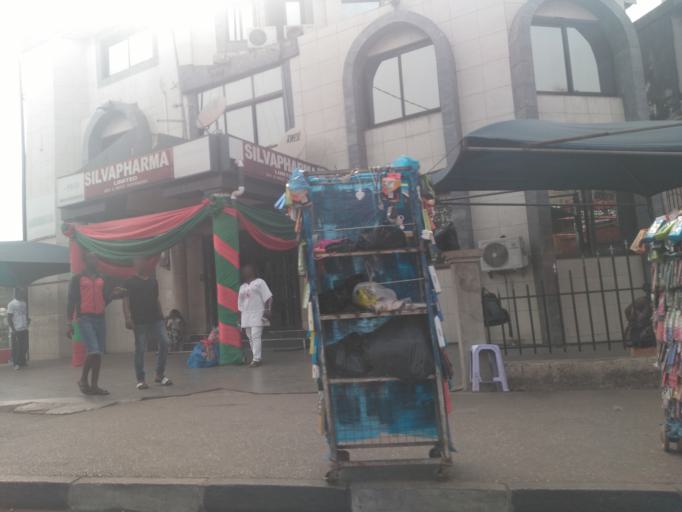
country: GH
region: Ashanti
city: Kumasi
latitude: 6.6986
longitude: -1.6315
